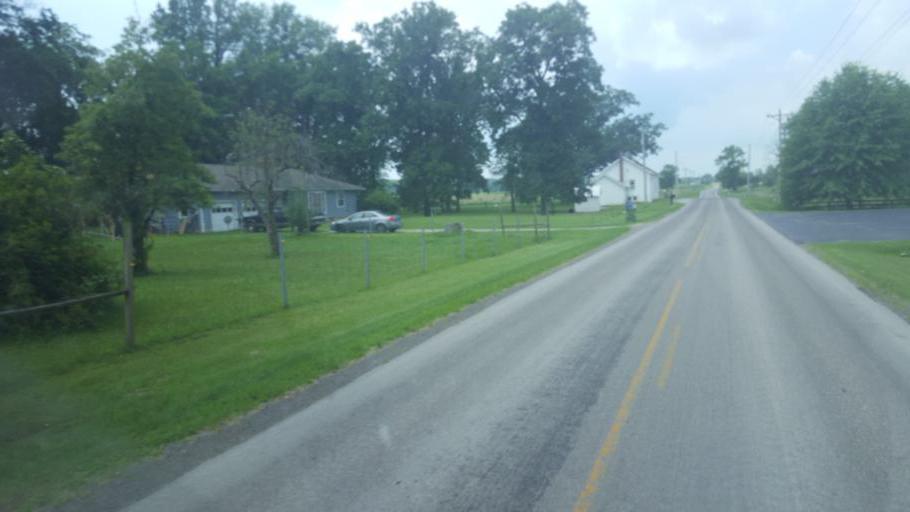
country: US
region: Ohio
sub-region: Hardin County
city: Kenton
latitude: 40.5878
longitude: -83.4725
